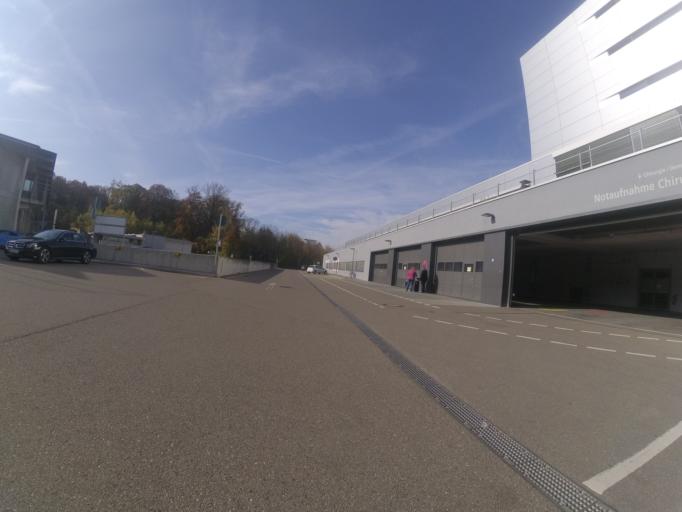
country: DE
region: Baden-Wuerttemberg
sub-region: Tuebingen Region
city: Dornstadt
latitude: 48.4220
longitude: 9.9516
